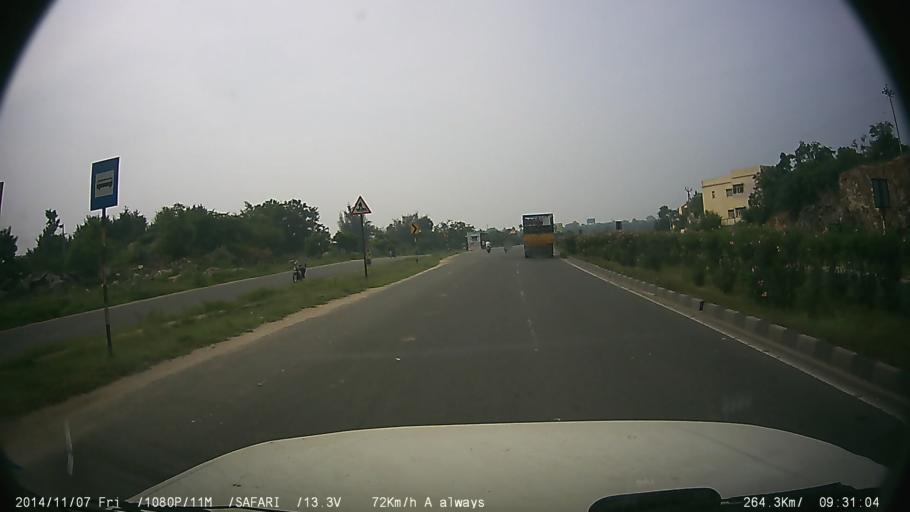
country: IN
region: Tamil Nadu
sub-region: Erode
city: Bhavani
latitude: 11.4179
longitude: 77.6766
